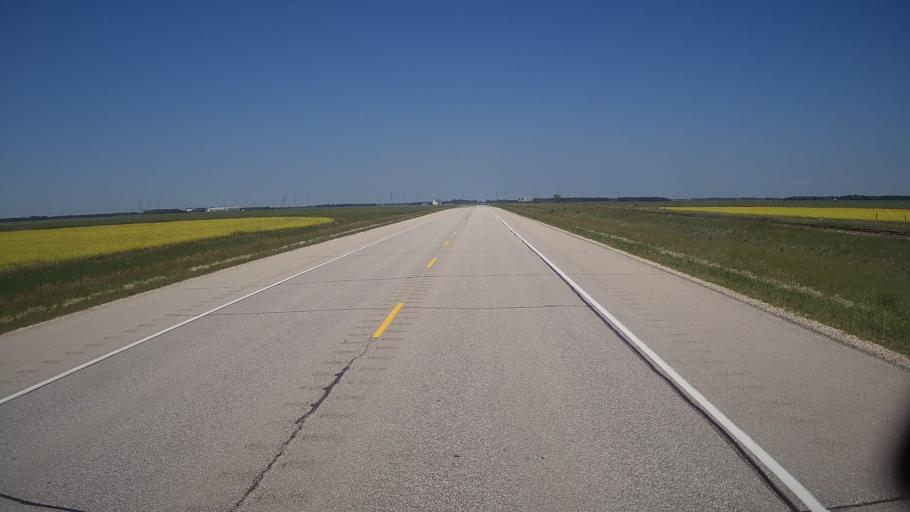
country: CA
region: Manitoba
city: Stonewall
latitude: 50.0360
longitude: -97.3994
